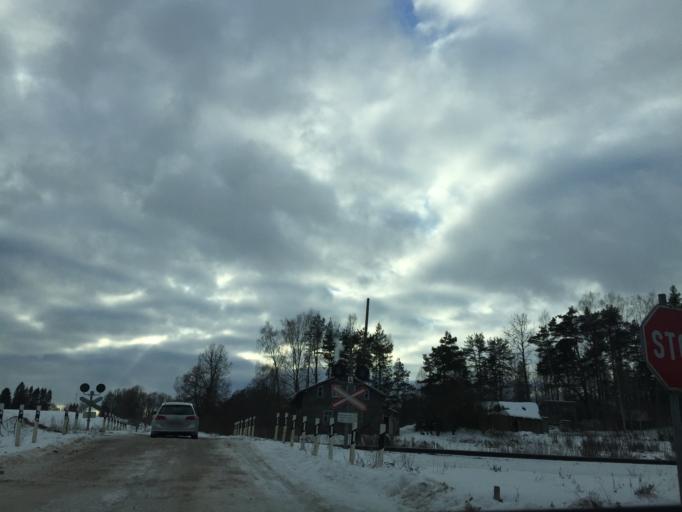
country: LV
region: Lielvarde
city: Lielvarde
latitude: 56.5814
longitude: 24.7350
